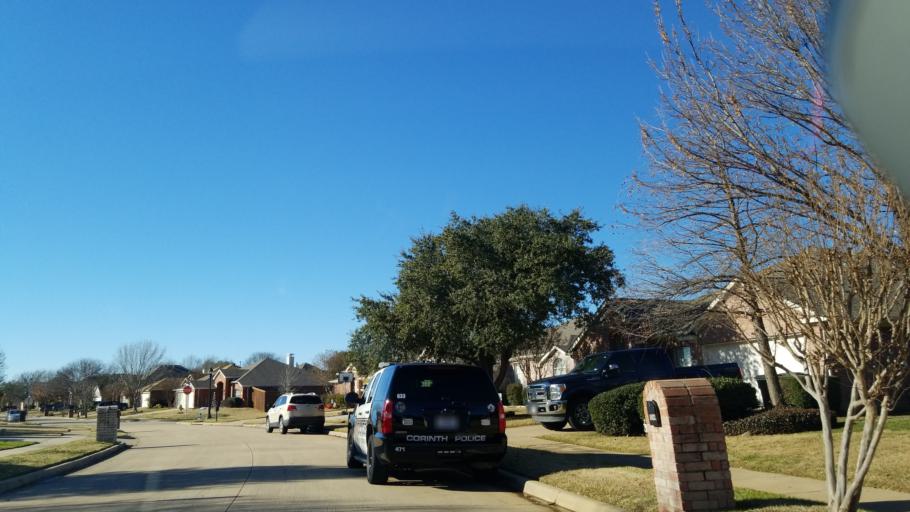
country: US
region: Texas
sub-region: Denton County
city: Corinth
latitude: 33.1377
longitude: -97.0847
